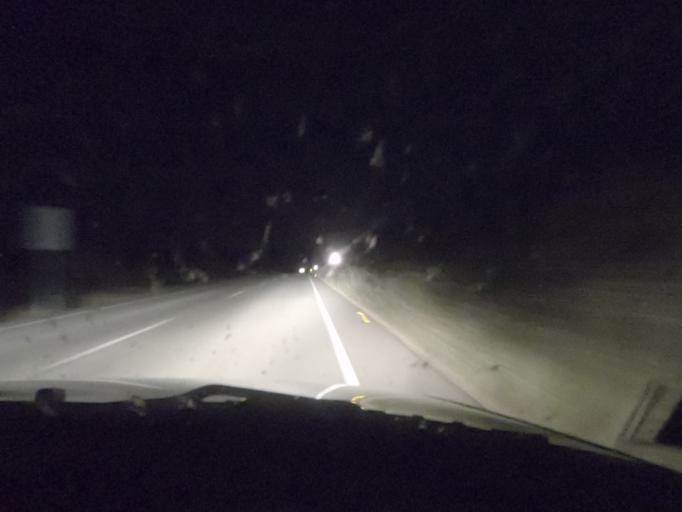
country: ES
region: Extremadura
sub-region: Provincia de Caceres
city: Perales del Puerto
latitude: 40.1136
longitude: -6.6705
